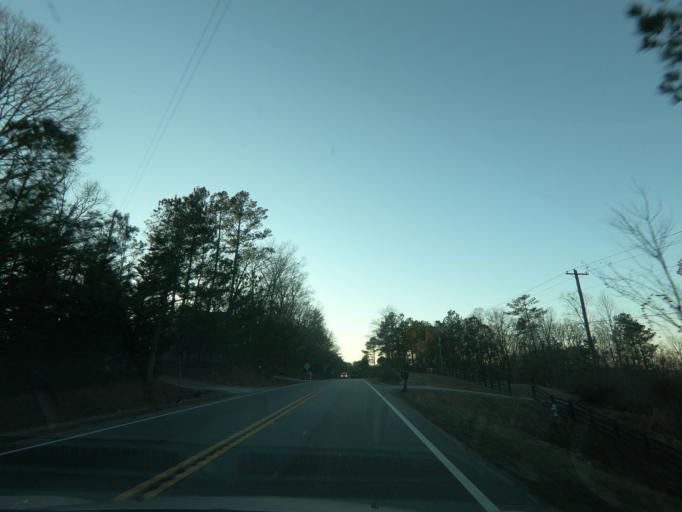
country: US
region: Georgia
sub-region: Cherokee County
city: Ball Ground
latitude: 34.2988
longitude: -84.2440
